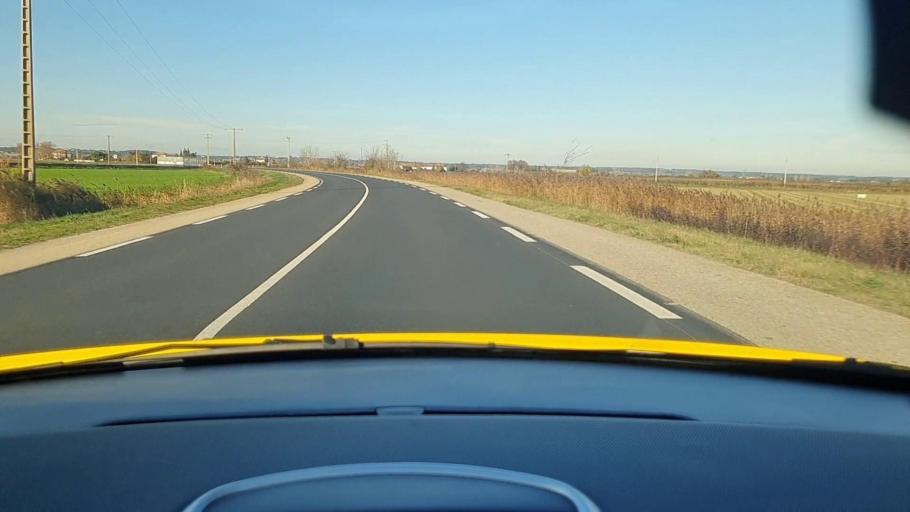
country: FR
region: Languedoc-Roussillon
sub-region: Departement du Gard
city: Bellegarde
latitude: 43.7206
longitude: 4.5479
